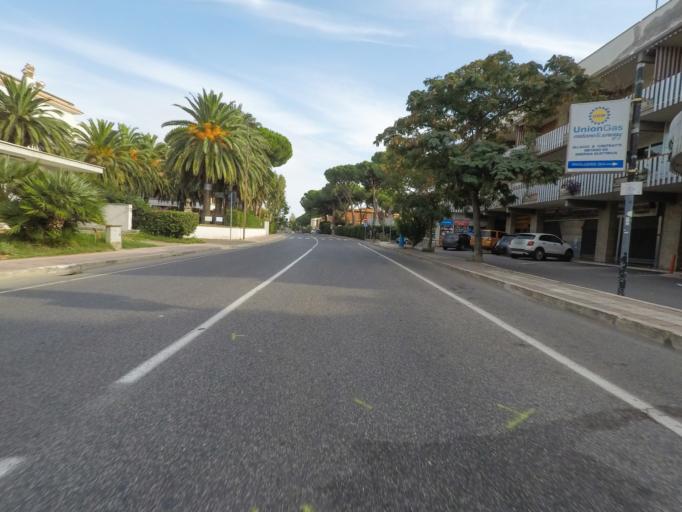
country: IT
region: Latium
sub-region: Citta metropolitana di Roma Capitale
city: Santa Marinella
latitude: 42.0330
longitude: 11.8380
